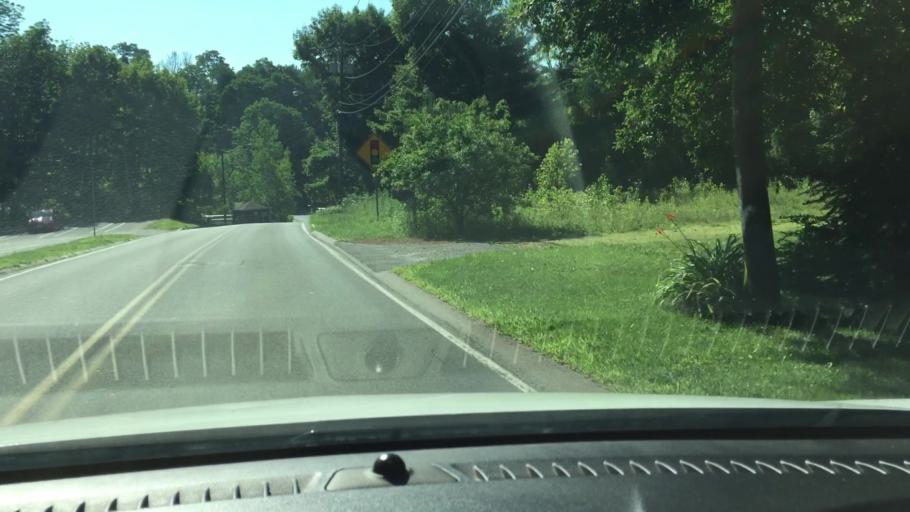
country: US
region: Massachusetts
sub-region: Berkshire County
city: Pittsfield
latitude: 42.4846
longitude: -73.2480
